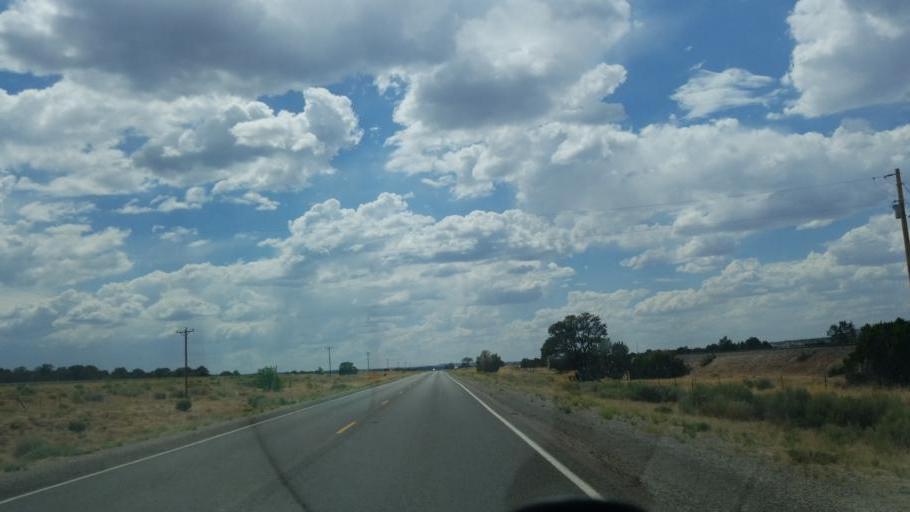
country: US
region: New Mexico
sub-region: McKinley County
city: Thoreau
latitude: 35.3895
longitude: -108.1756
